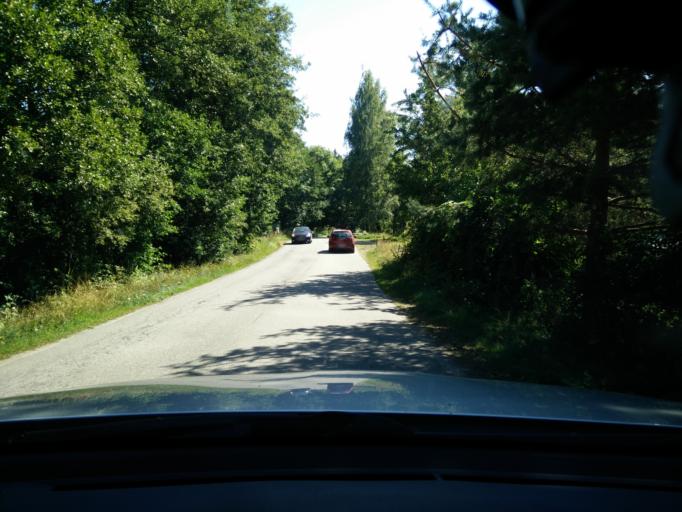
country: SE
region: OEstergoetland
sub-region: Norrkopings Kommun
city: Jursla
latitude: 58.7202
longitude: 16.1534
